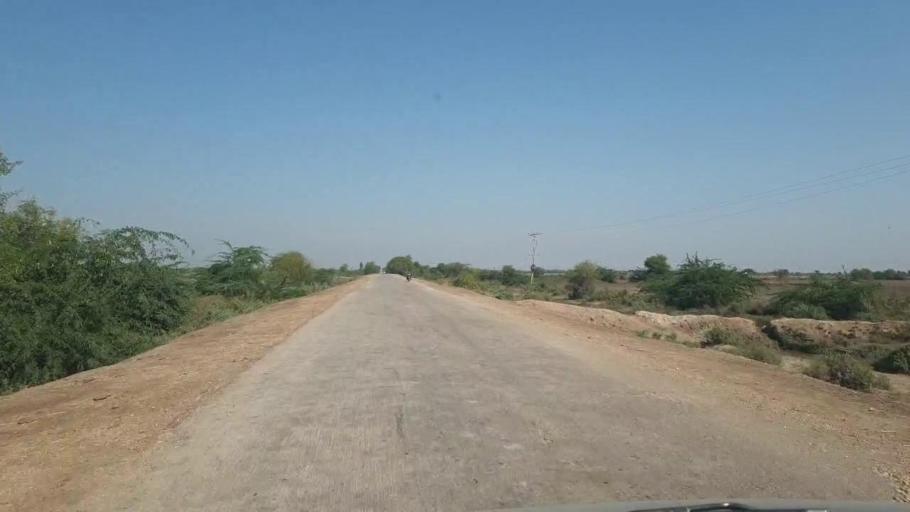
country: PK
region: Sindh
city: Tando Bago
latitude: 24.8086
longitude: 68.9805
